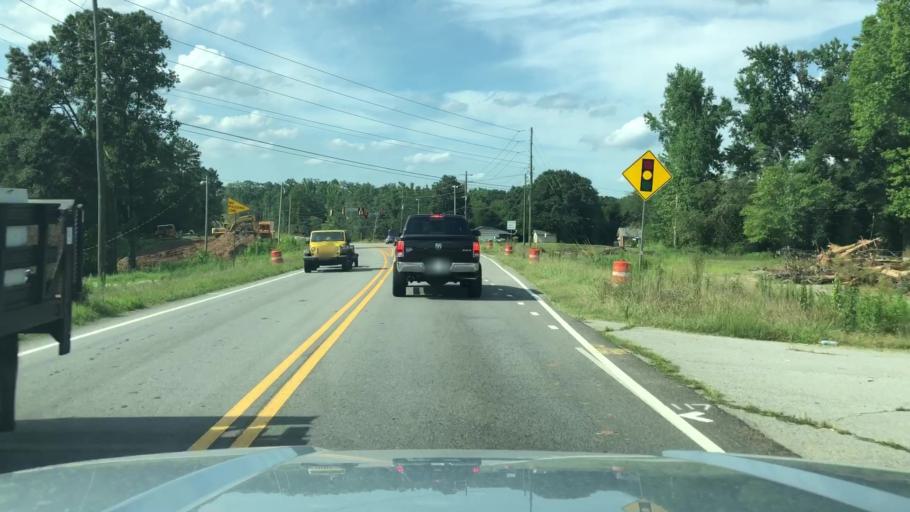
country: US
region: Georgia
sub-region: Paulding County
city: Hiram
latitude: 33.8498
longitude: -84.7565
